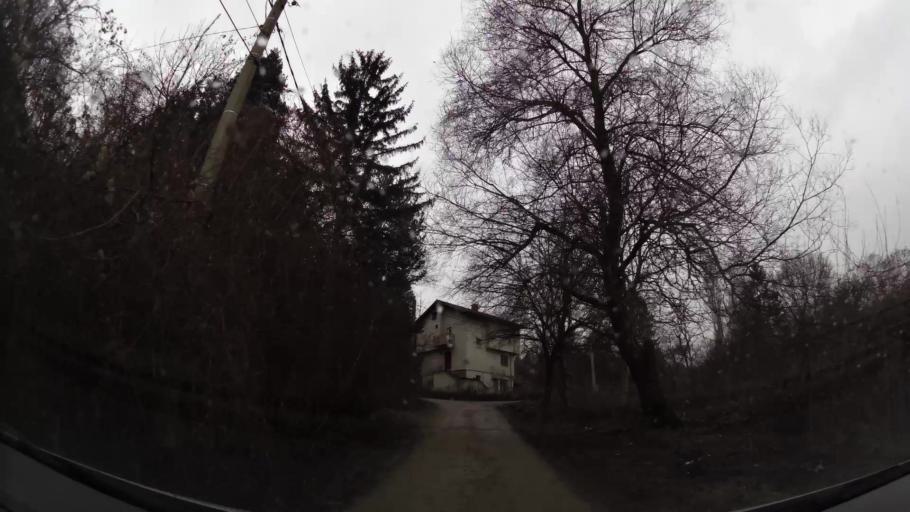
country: BG
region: Sofia-Capital
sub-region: Stolichna Obshtina
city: Sofia
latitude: 42.6033
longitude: 23.3875
